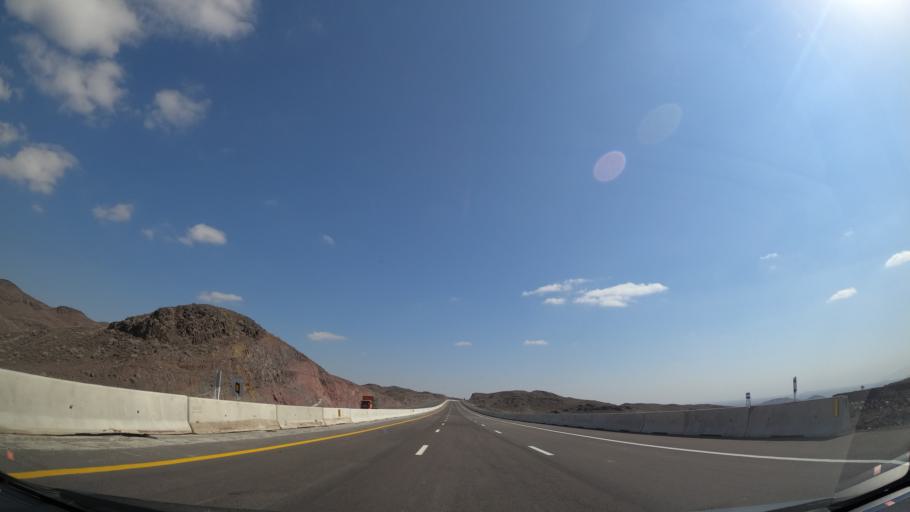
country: IR
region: Alborz
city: Eshtehard
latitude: 35.6629
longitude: 50.6522
